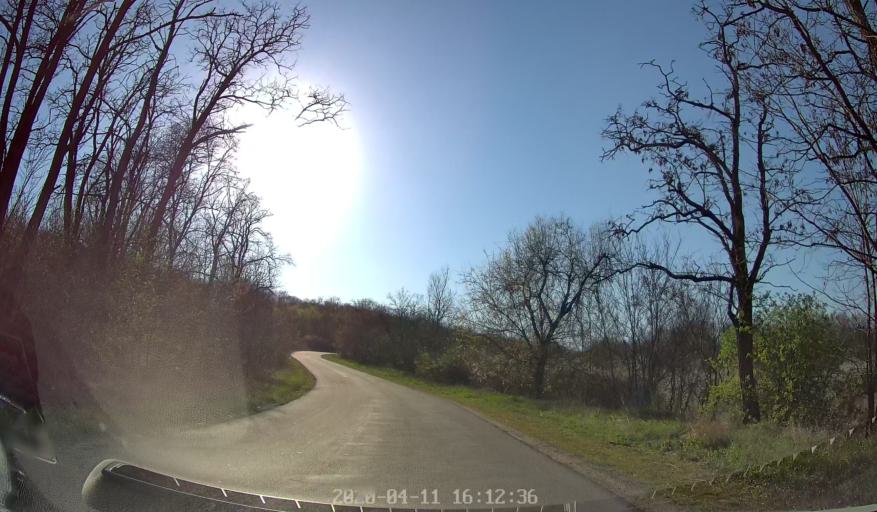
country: MD
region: Chisinau
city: Vadul lui Voda
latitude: 47.0701
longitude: 29.1201
